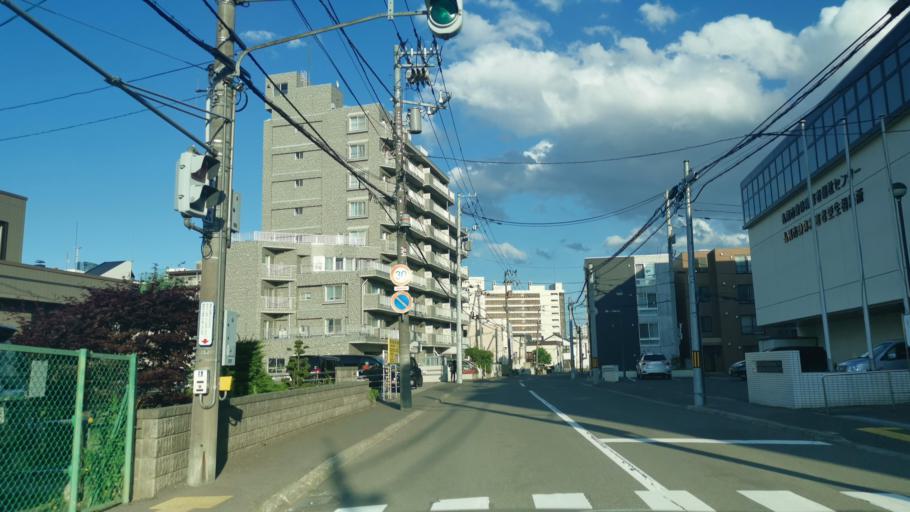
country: JP
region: Hokkaido
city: Sapporo
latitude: 43.0697
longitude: 141.3123
